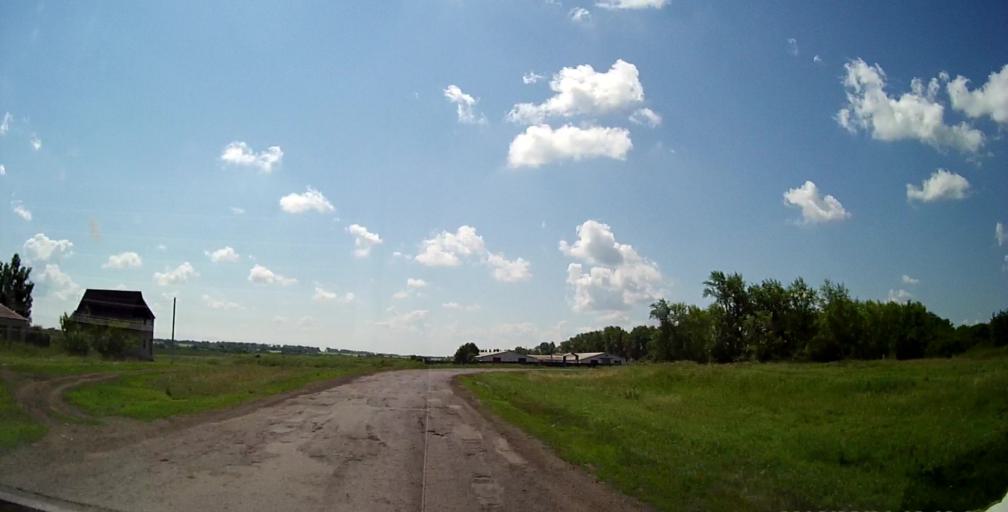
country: RU
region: Lipetsk
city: Chaplygin
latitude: 53.3170
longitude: 39.9596
